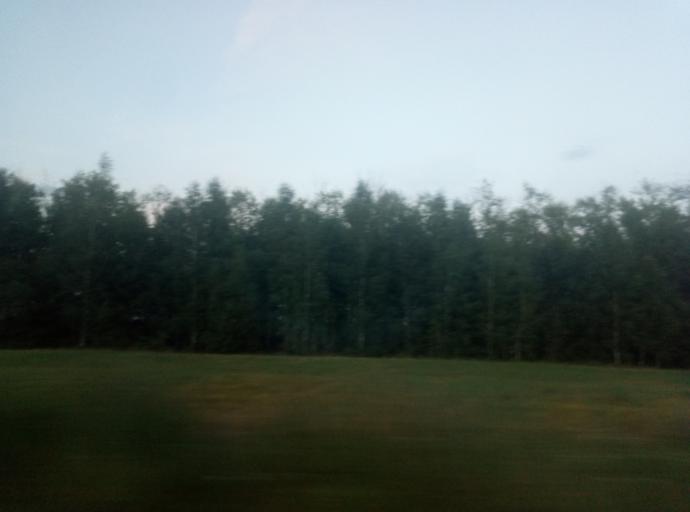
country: RU
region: Tula
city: Kireyevsk
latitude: 53.8543
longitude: 37.8785
